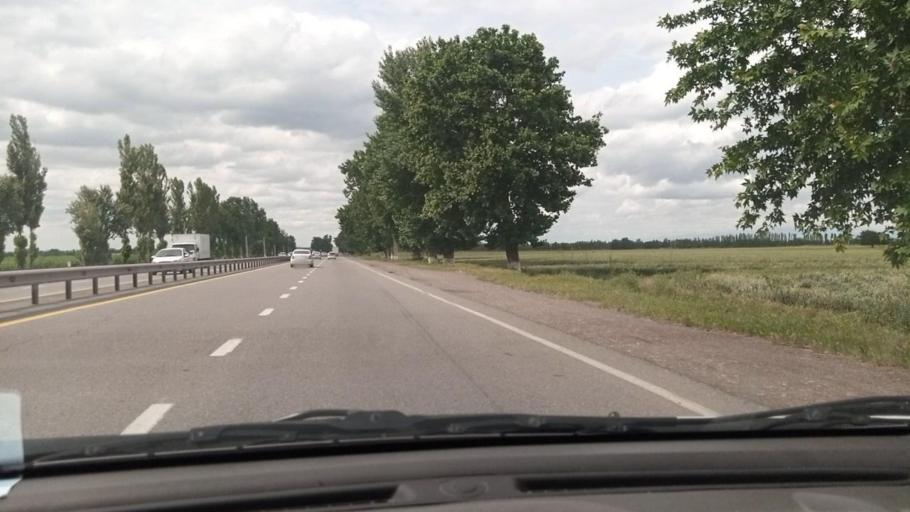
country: UZ
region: Toshkent Shahri
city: Bektemir
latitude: 41.1385
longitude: 69.4339
